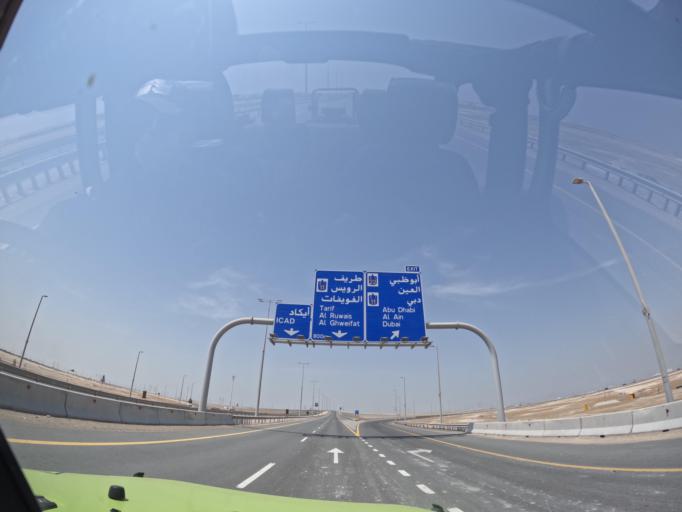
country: AE
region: Abu Dhabi
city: Abu Dhabi
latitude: 24.2426
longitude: 54.4784
